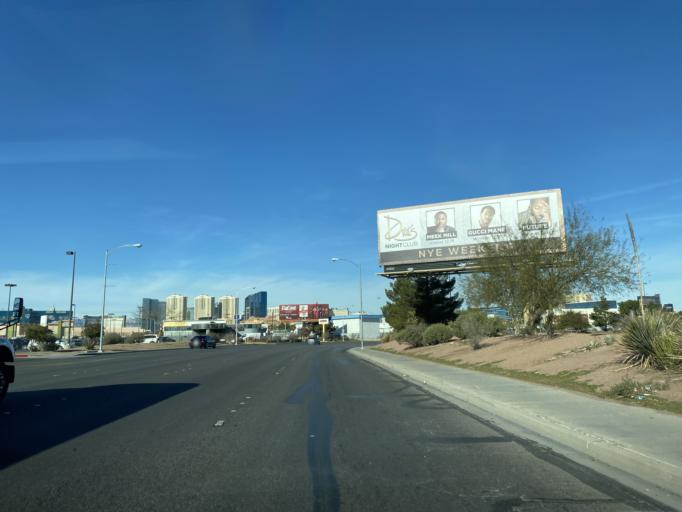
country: US
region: Nevada
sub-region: Clark County
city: Paradise
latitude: 36.1032
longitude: -115.1480
